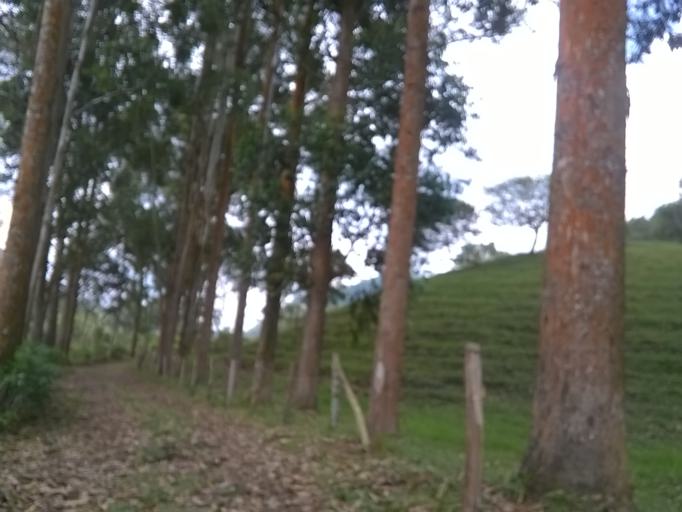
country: CO
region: Quindio
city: Salento
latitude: 4.6497
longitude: -75.5871
